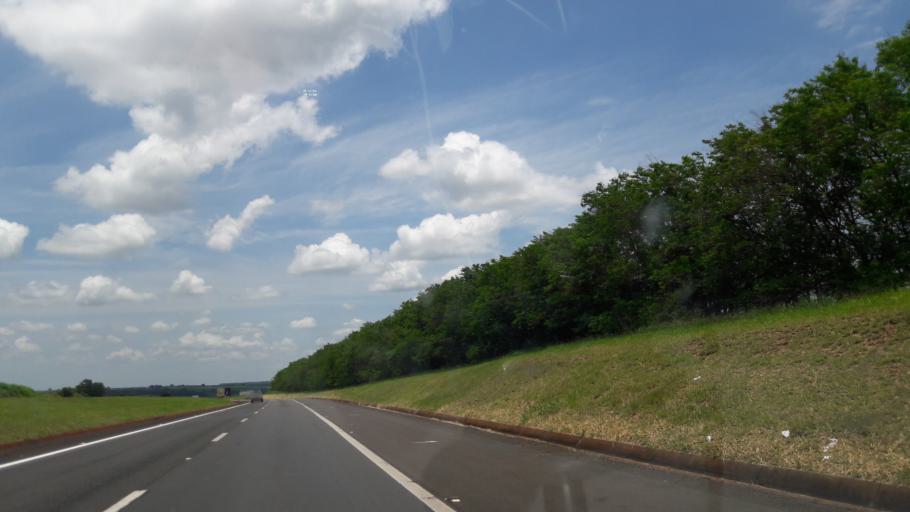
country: BR
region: Sao Paulo
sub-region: Avare
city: Avare
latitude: -22.9570
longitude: -48.8185
